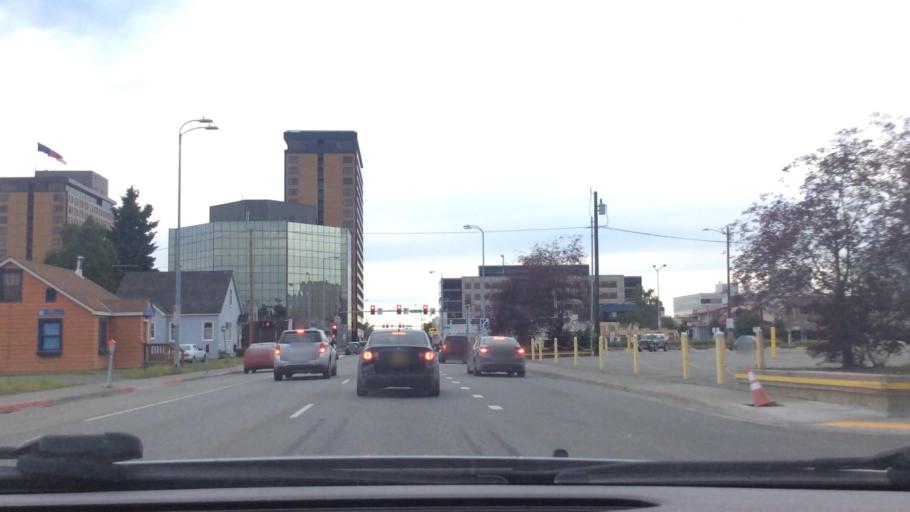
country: US
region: Alaska
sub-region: Anchorage Municipality
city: Anchorage
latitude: 61.2156
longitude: -149.8995
